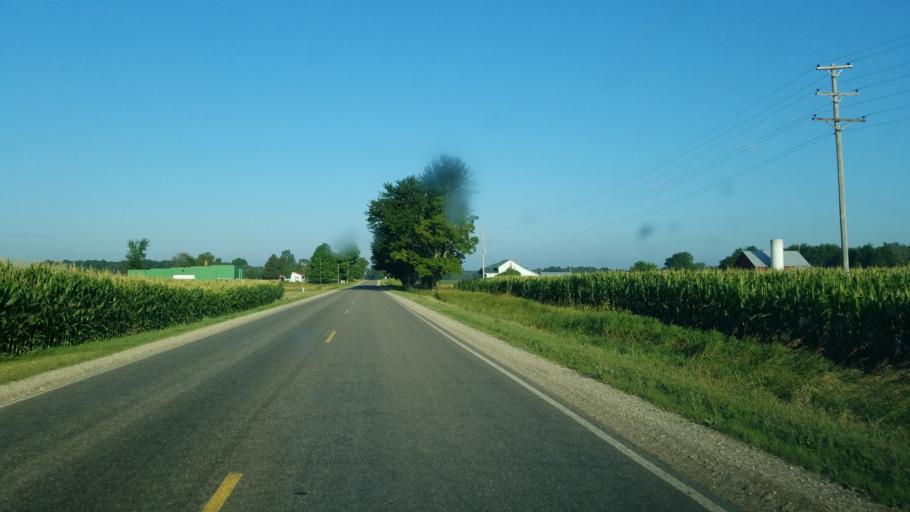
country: US
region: Michigan
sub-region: Mecosta County
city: Canadian Lakes
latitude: 43.5398
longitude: -85.2356
